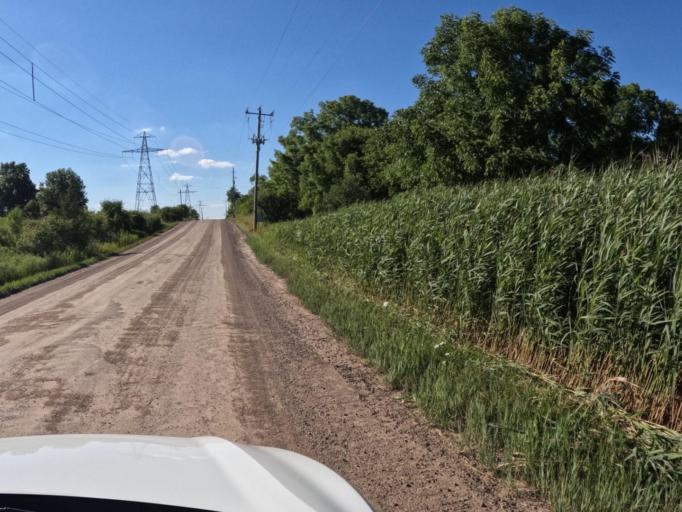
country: CA
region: Ontario
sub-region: Wellington County
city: Guelph
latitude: 43.4415
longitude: -80.1450
